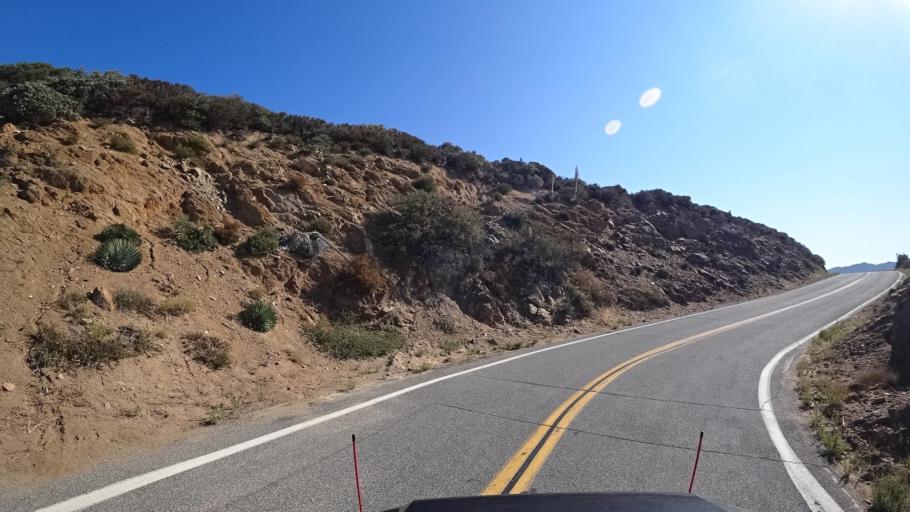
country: US
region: California
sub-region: San Diego County
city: Pine Valley
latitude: 32.9360
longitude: -116.4868
